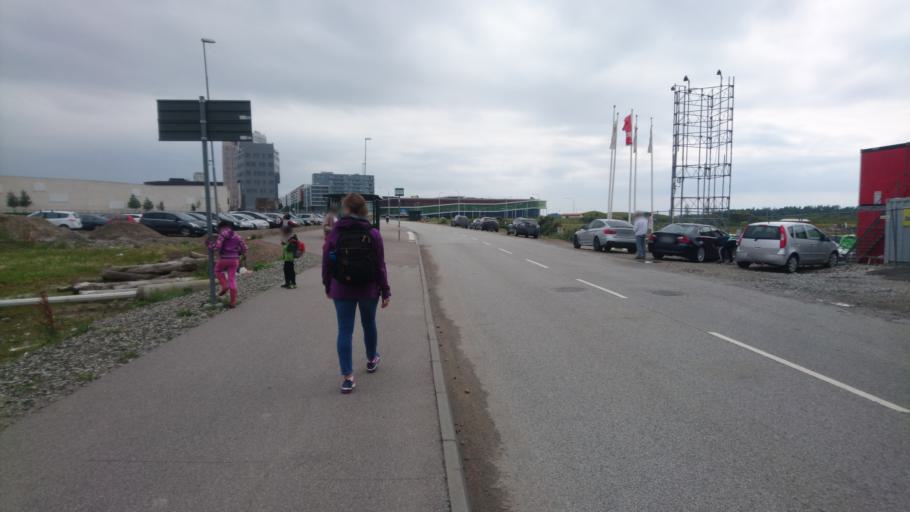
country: SE
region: Skane
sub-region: Malmo
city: Malmoe
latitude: 55.5696
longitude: 12.9764
